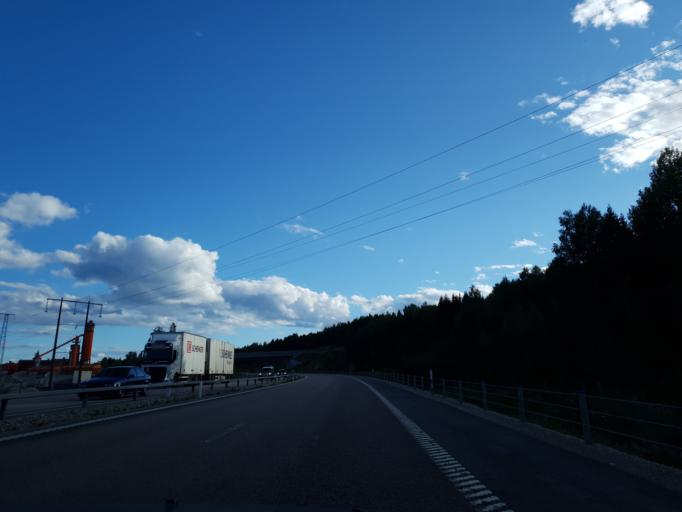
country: SE
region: Vaesternorrland
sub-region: Sundsvalls Kommun
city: Stockvik
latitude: 62.3224
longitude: 17.3410
